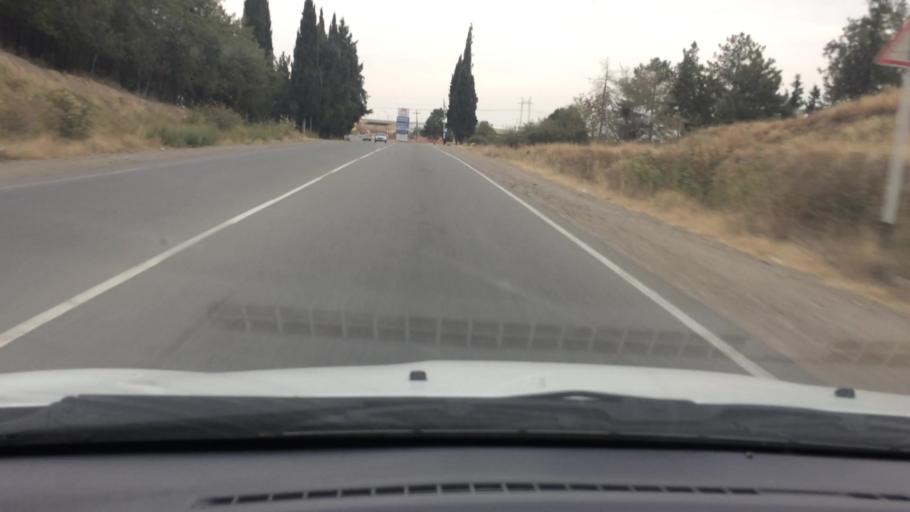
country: GE
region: Kvemo Kartli
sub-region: Marneuli
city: Marneuli
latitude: 41.5234
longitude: 44.7781
